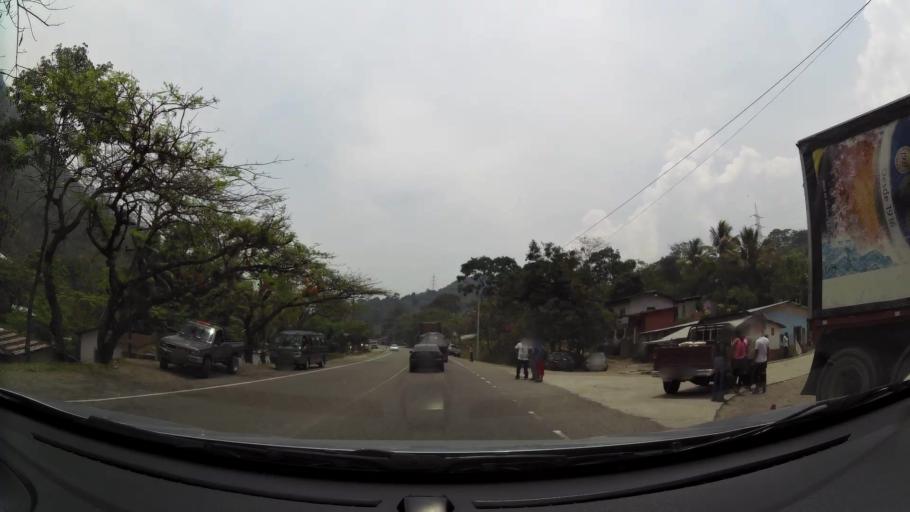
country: HN
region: Comayagua
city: Taulabe
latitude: 14.7479
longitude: -87.9596
